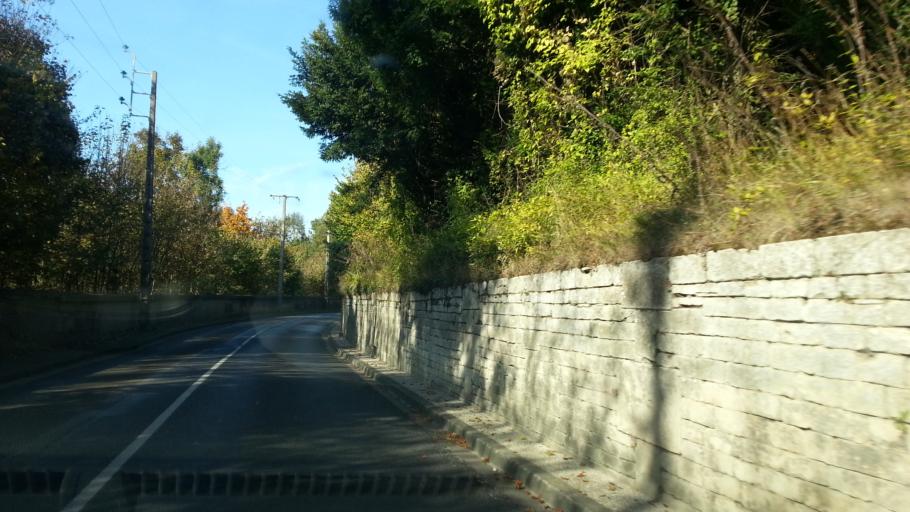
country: FR
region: Picardie
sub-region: Departement de l'Oise
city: Cires-les-Mello
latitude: 49.2683
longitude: 2.3665
